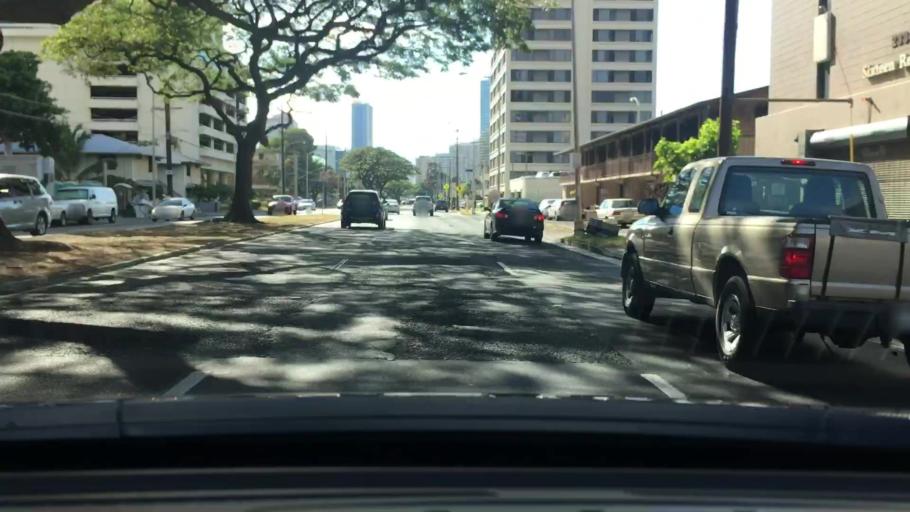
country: US
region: Hawaii
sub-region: Honolulu County
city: Honolulu
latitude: 21.2881
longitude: -157.8282
